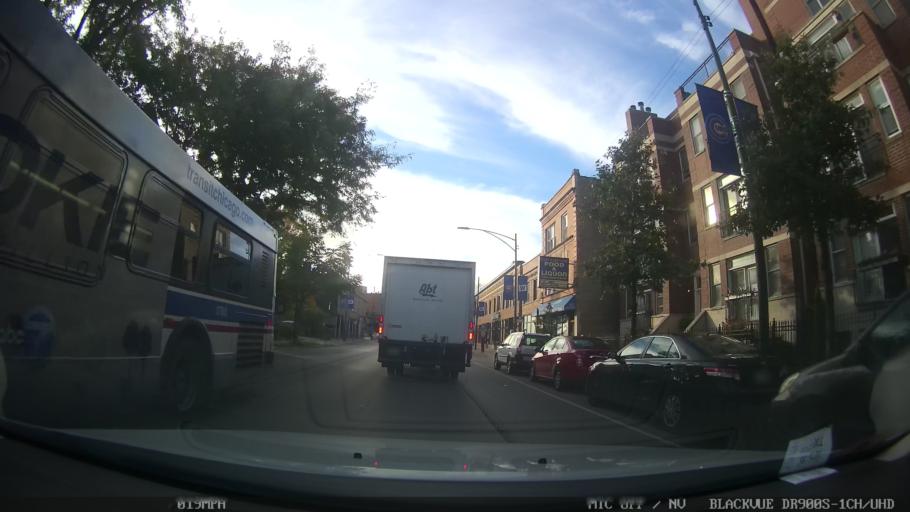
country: US
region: Illinois
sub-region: Cook County
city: Lincolnwood
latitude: 41.9518
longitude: -87.6603
